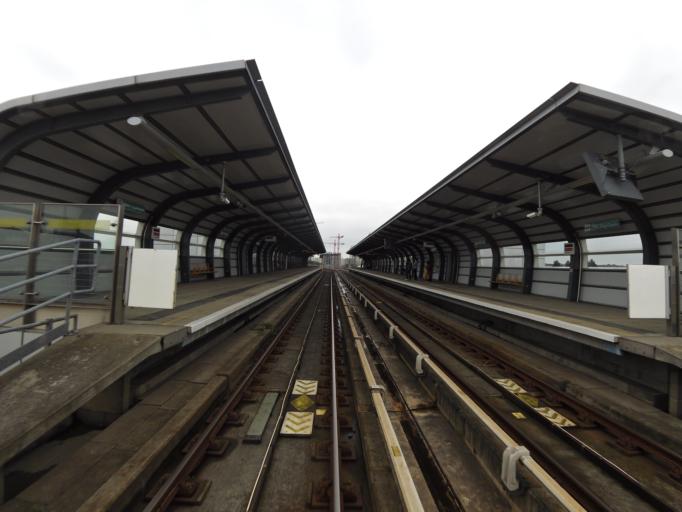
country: GB
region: England
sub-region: Greater London
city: Poplar
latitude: 51.5029
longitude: 0.0222
